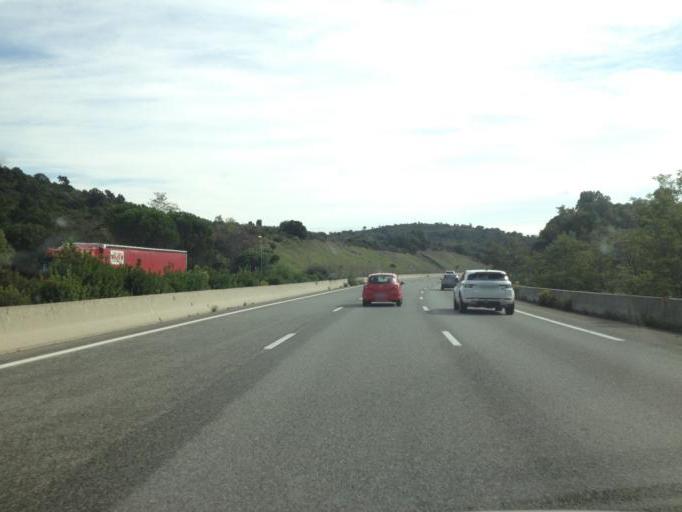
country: FR
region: Provence-Alpes-Cote d'Azur
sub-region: Departement du Var
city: Tanneron
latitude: 43.5395
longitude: 6.8493
